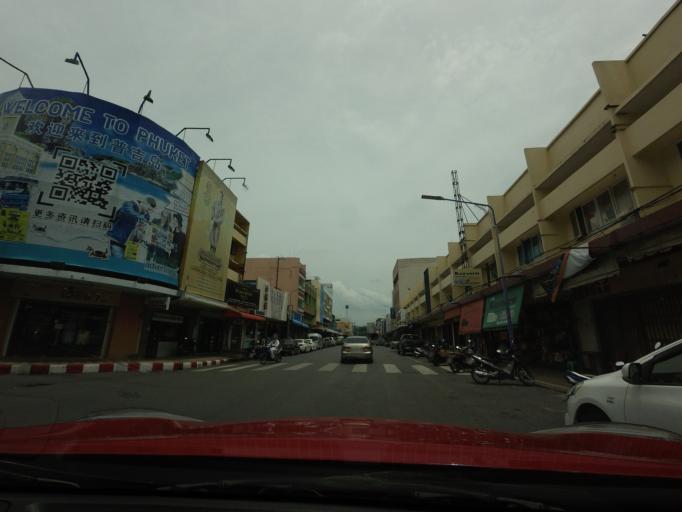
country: TH
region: Songkhla
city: Hat Yai
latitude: 7.0003
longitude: 100.4713
